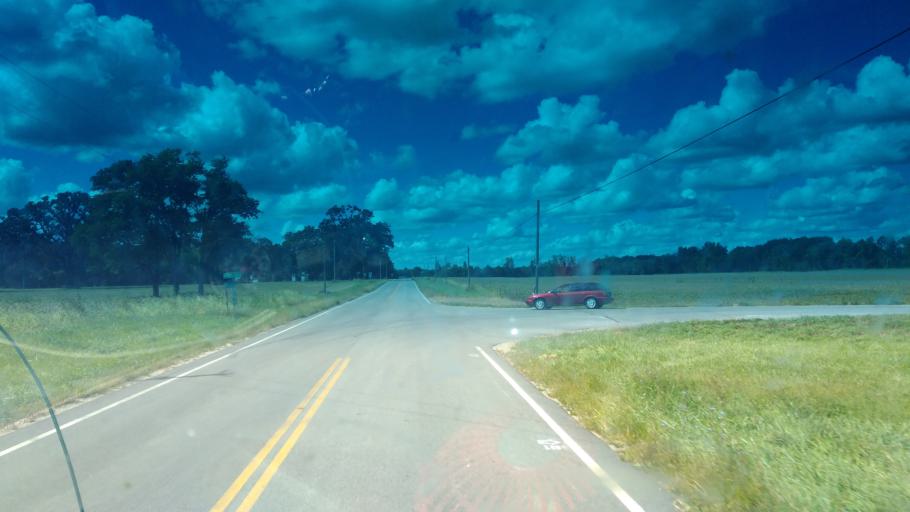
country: US
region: Ohio
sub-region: Champaign County
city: North Lewisburg
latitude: 40.2077
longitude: -83.4927
